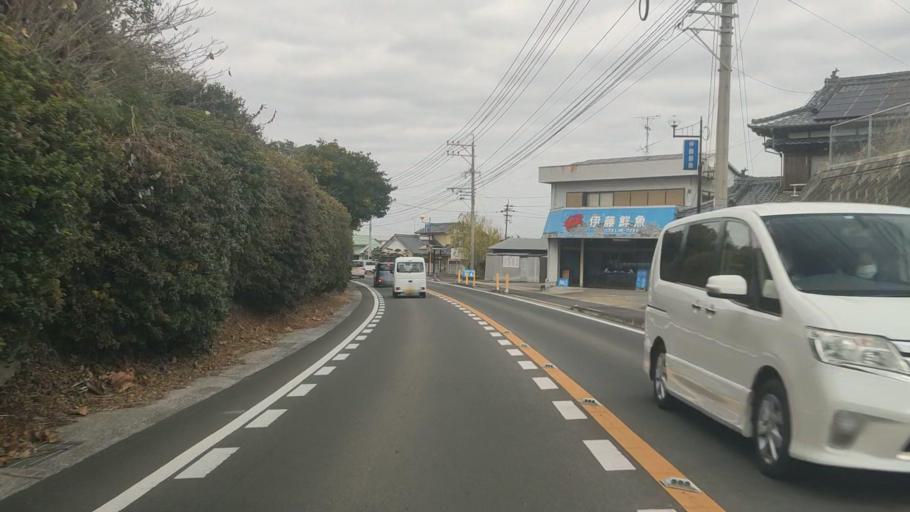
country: JP
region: Nagasaki
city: Shimabara
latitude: 32.8545
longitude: 130.3382
